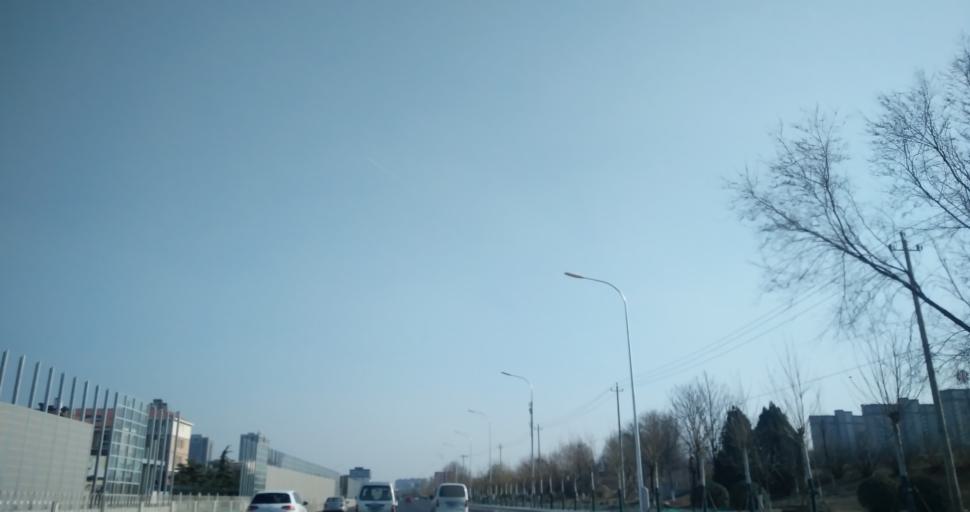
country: CN
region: Beijing
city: Jiugong
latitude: 39.7888
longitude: 116.4817
